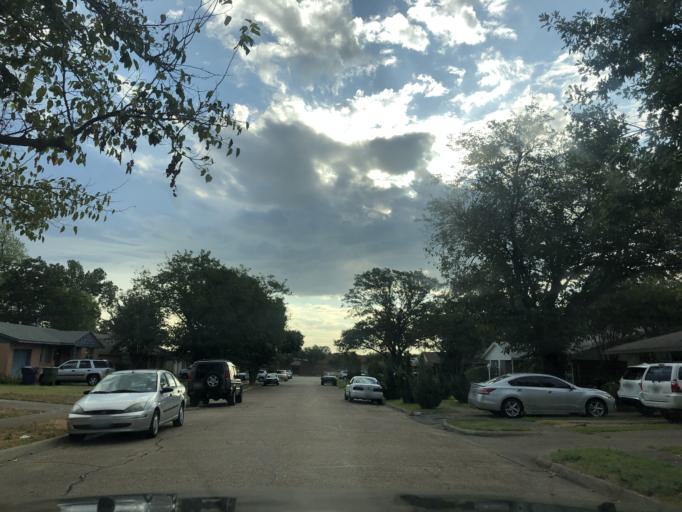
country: US
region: Texas
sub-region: Dallas County
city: Garland
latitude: 32.8762
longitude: -96.6501
